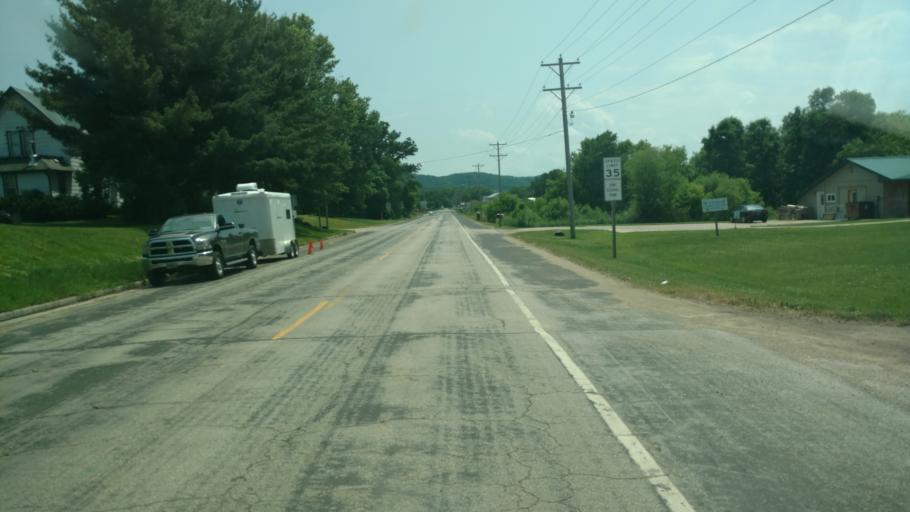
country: US
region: Wisconsin
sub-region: Monroe County
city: Cashton
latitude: 43.5787
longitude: -90.6414
